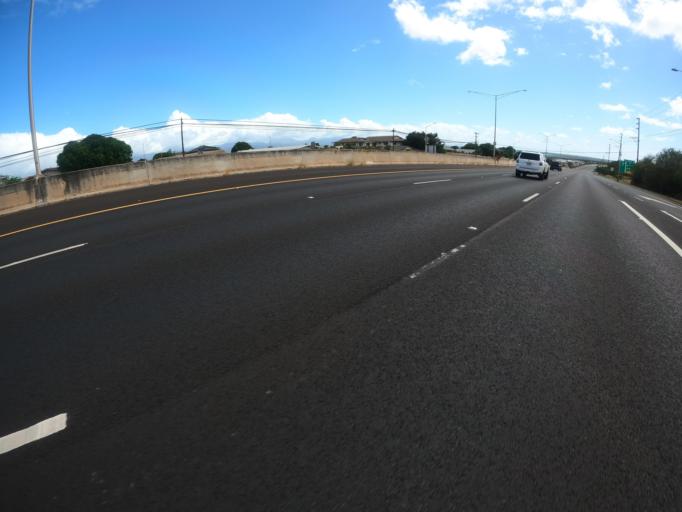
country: US
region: Hawaii
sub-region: Honolulu County
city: Royal Kunia
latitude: 21.3824
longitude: -158.0312
